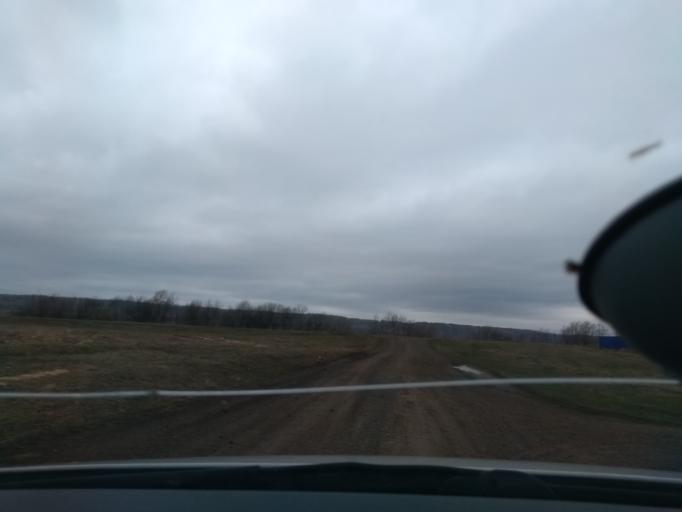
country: RU
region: Perm
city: Orda
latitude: 57.2246
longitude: 56.6000
